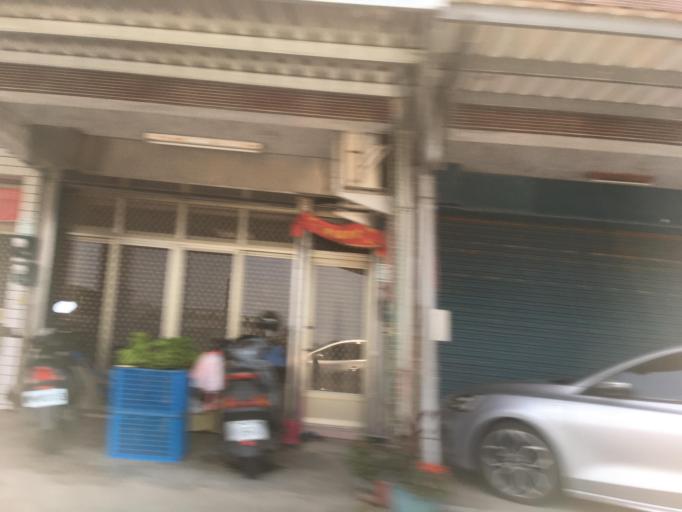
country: TW
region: Taiwan
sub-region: Yilan
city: Yilan
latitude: 24.6489
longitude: 121.7639
